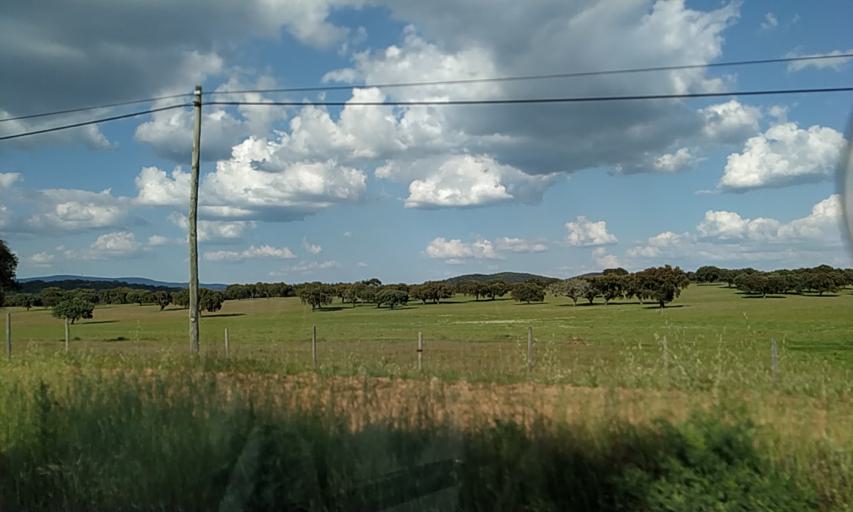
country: PT
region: Portalegre
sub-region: Portalegre
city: Urra
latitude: 39.1932
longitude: -7.4570
